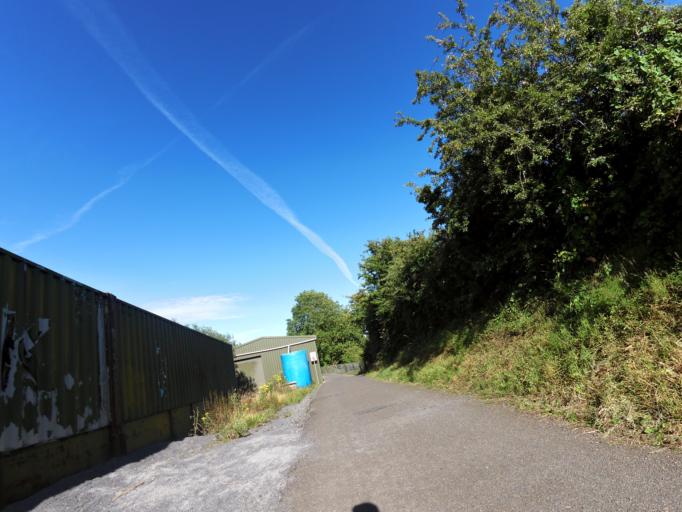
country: IE
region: Leinster
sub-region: Kilkenny
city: Mooncoin
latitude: 52.2463
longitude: -7.2525
